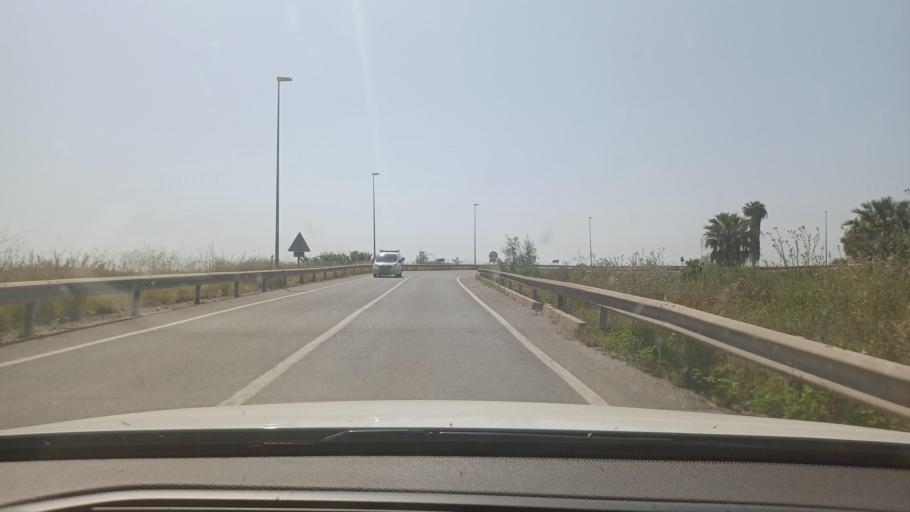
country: ES
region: Valencia
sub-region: Provincia de Alicante
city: Dolores
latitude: 38.1249
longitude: -0.7790
